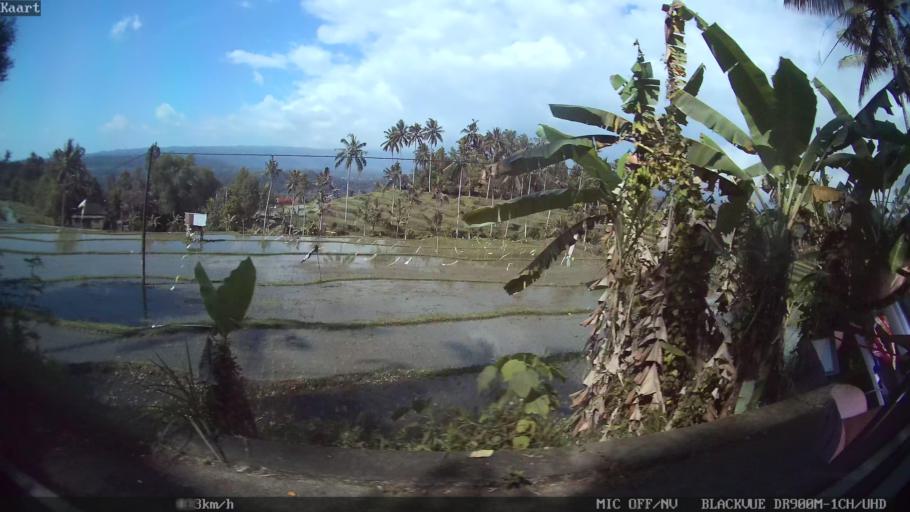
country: ID
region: Bali
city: Subuk
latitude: -8.2935
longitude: 114.9735
